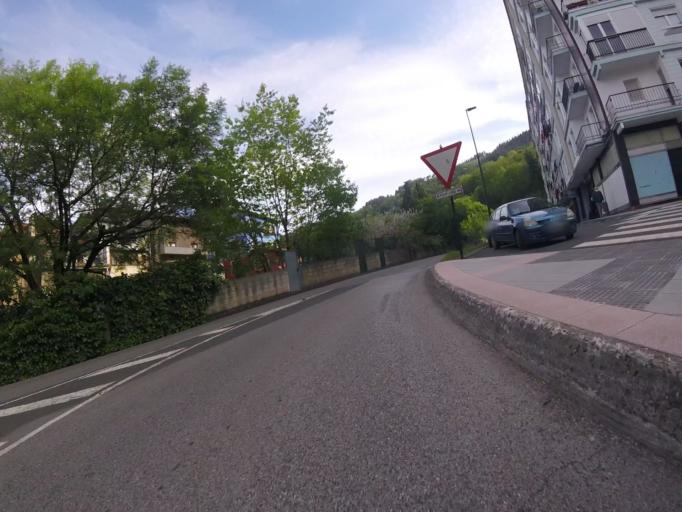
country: ES
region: Basque Country
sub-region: Provincia de Guipuzcoa
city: Zumarraga
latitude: 43.0911
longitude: -2.3129
